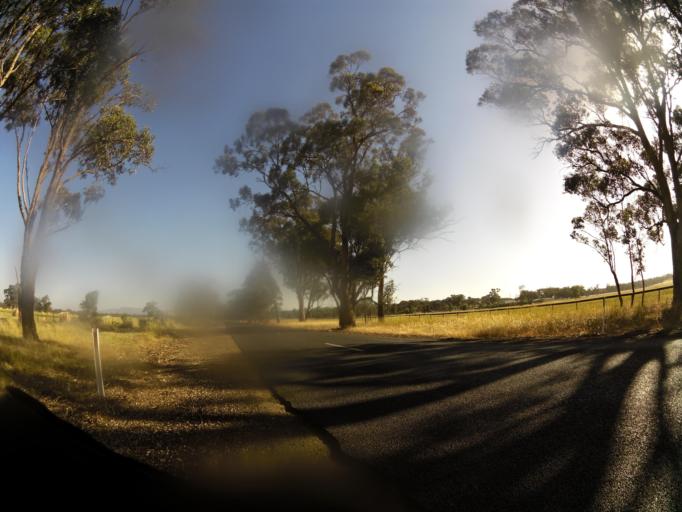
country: AU
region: Victoria
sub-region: Murrindindi
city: Kinglake West
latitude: -36.9812
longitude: 145.1109
